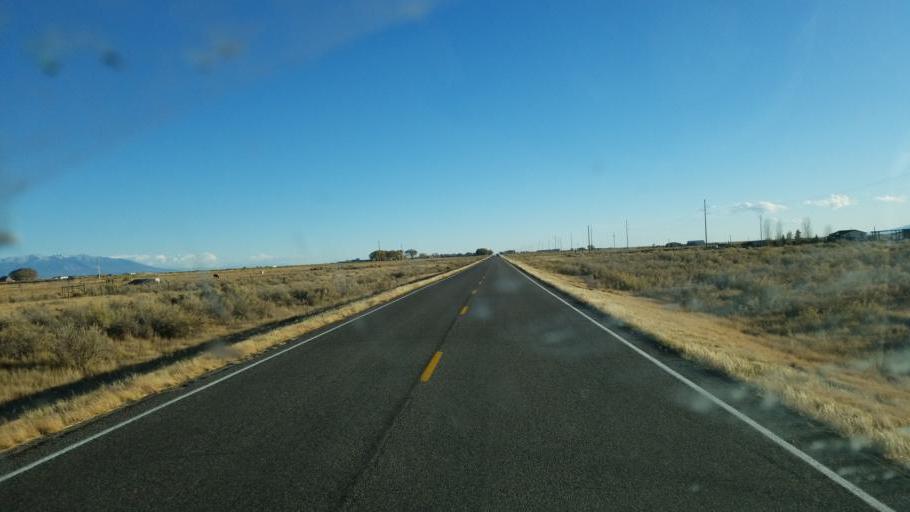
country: US
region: Colorado
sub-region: Saguache County
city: Saguache
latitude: 38.0304
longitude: -105.9120
